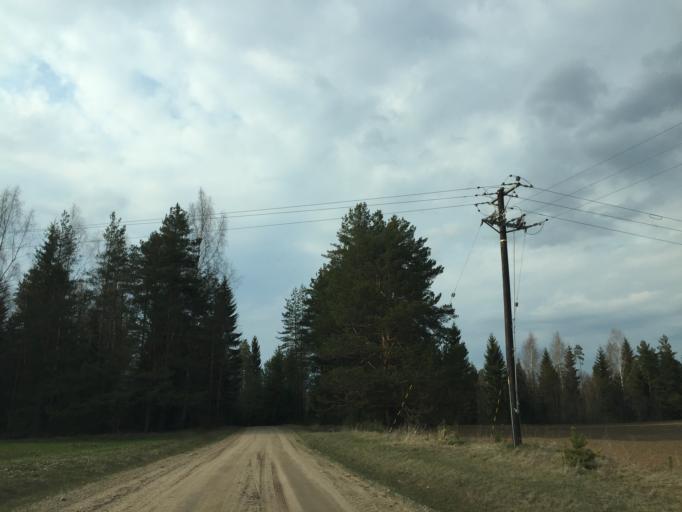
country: EE
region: Vorumaa
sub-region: Antsla vald
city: Vana-Antsla
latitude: 57.9591
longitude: 26.6954
